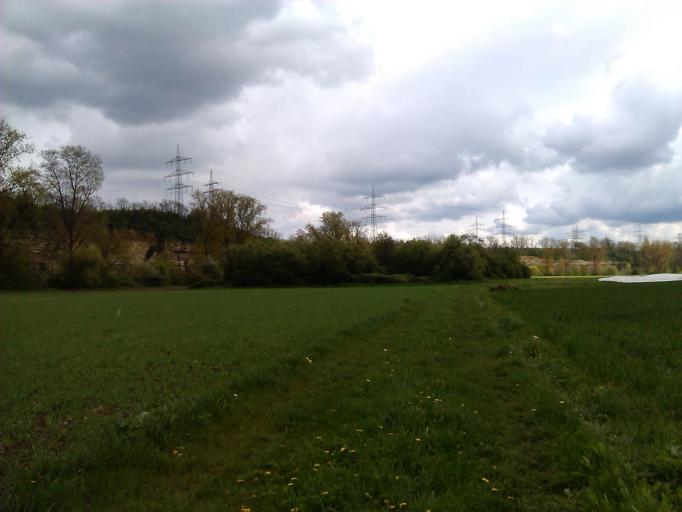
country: DE
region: Baden-Wuerttemberg
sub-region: Regierungsbezirk Stuttgart
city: Talheim
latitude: 49.0898
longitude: 9.1723
